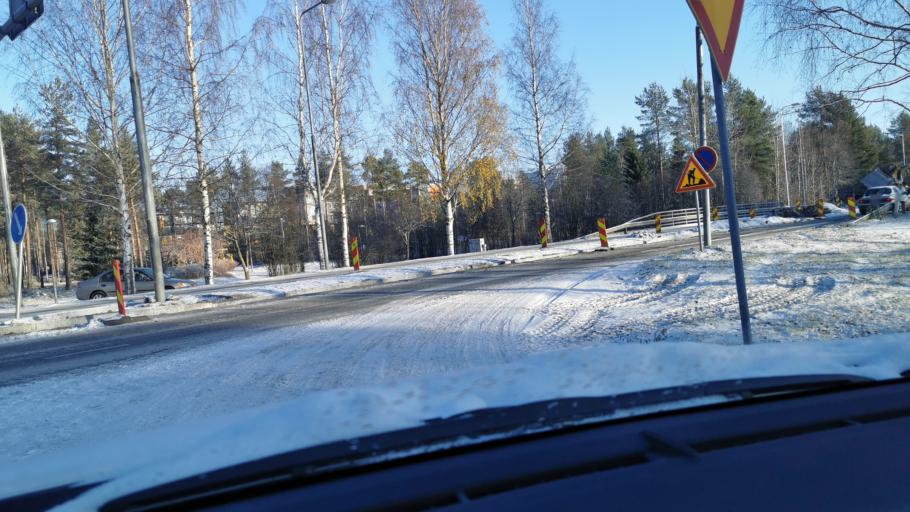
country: FI
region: Northern Ostrobothnia
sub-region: Oulu
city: Oulu
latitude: 65.0555
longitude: 25.4695
